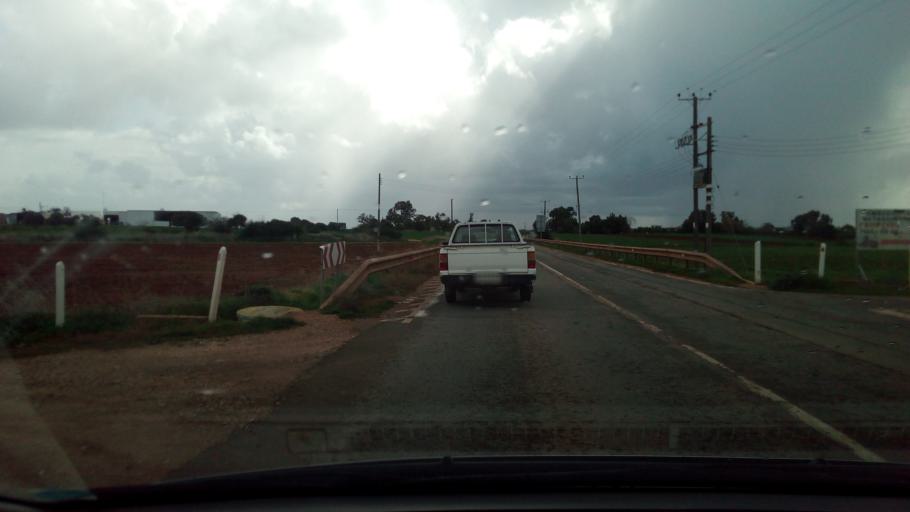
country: CY
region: Ammochostos
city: Liopetri
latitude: 34.9960
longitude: 33.8921
